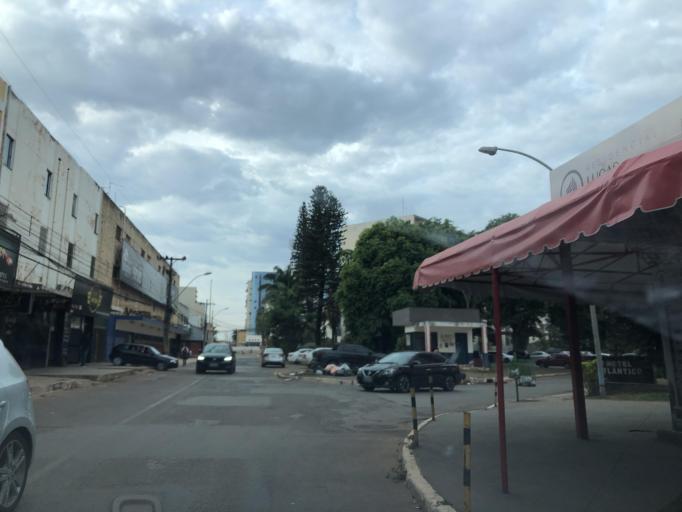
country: BR
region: Federal District
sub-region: Brasilia
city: Brasilia
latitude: -15.8338
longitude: -48.0522
